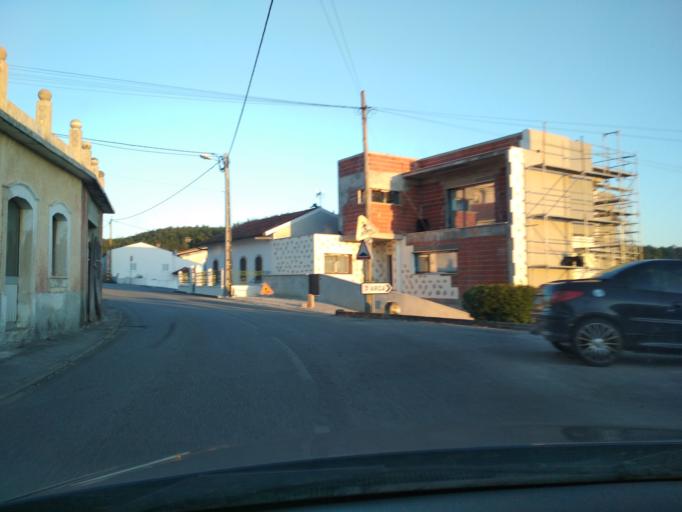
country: PT
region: Coimbra
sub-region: Condeixa-A-Nova
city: Condeixa-a-Nova
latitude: 40.1695
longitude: -8.4785
